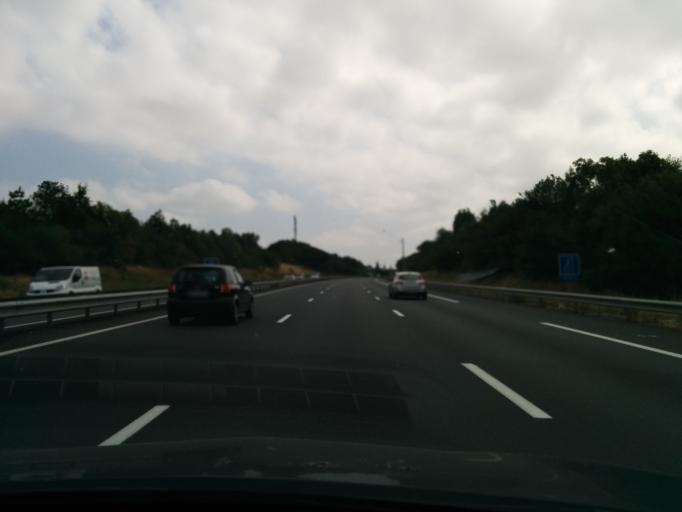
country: FR
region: Midi-Pyrenees
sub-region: Departement de la Haute-Garonne
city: Montrabe
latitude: 43.6517
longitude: 1.5186
